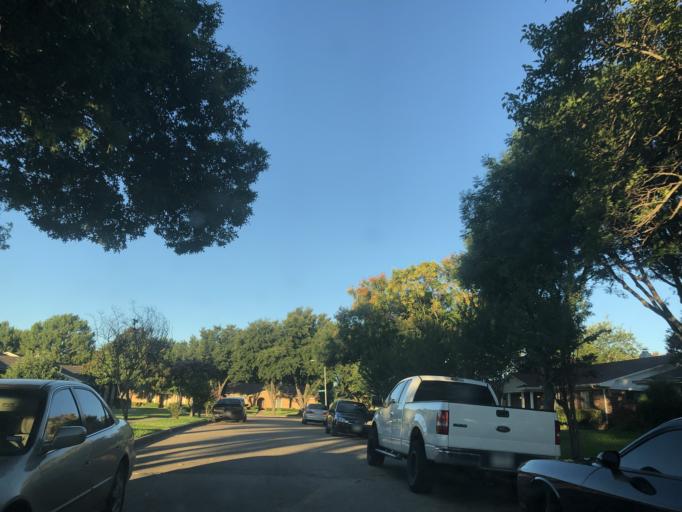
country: US
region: Texas
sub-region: Dallas County
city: Garland
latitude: 32.8351
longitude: -96.6373
